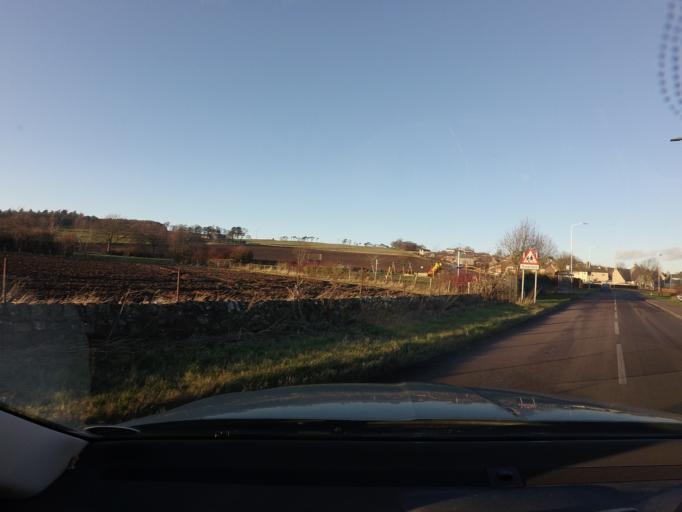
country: GB
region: Scotland
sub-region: Fife
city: Tayport
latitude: 56.4421
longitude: -2.8842
